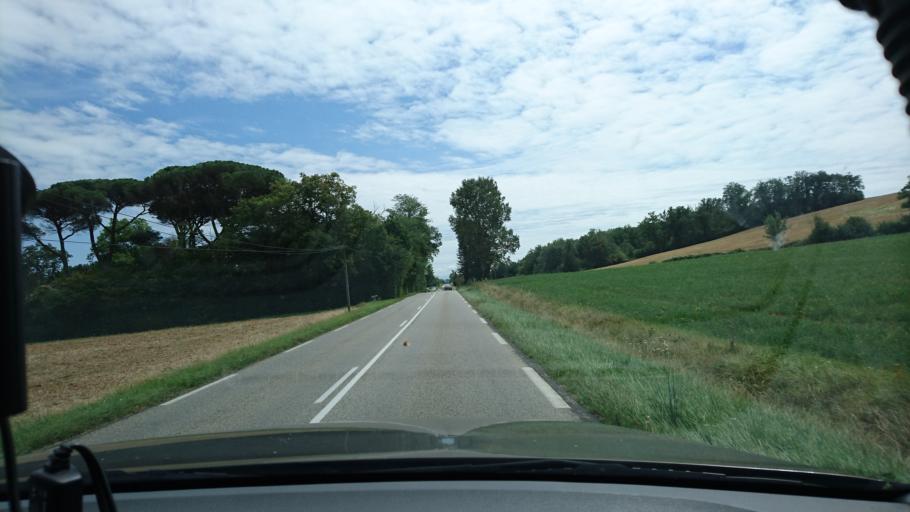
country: FR
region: Midi-Pyrenees
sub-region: Departement de la Haute-Garonne
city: Saint-Sulpice-sur-Leze
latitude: 43.3050
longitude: 1.3315
